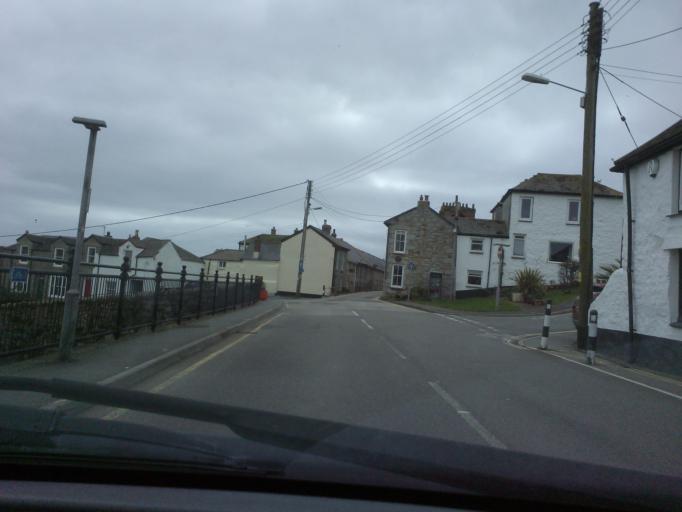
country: GB
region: England
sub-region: Cornwall
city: Penzance
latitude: 50.1015
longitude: -5.5461
